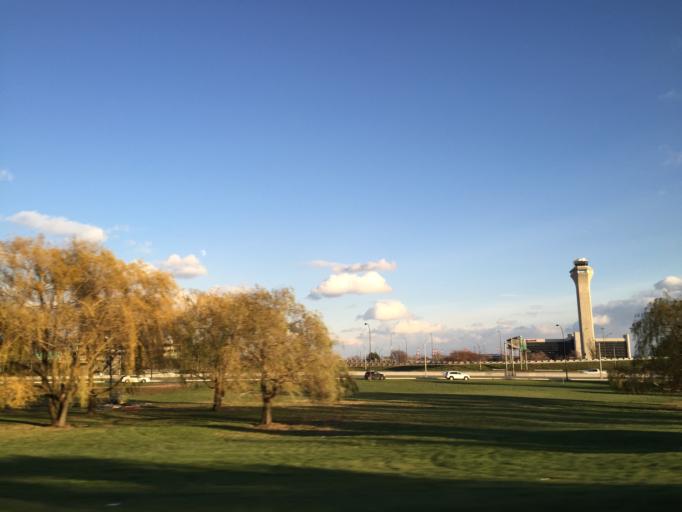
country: US
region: New Jersey
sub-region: Union County
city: Elizabeth
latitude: 40.6955
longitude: -74.1884
